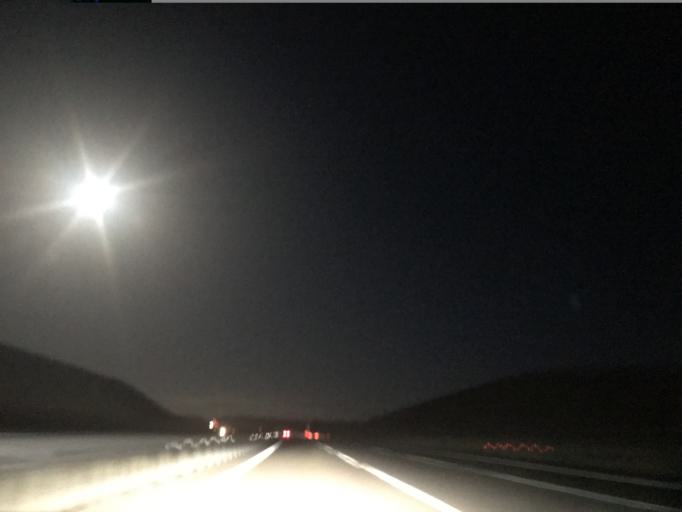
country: TR
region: Nigde
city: Ulukisla
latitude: 37.6413
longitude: 34.3809
